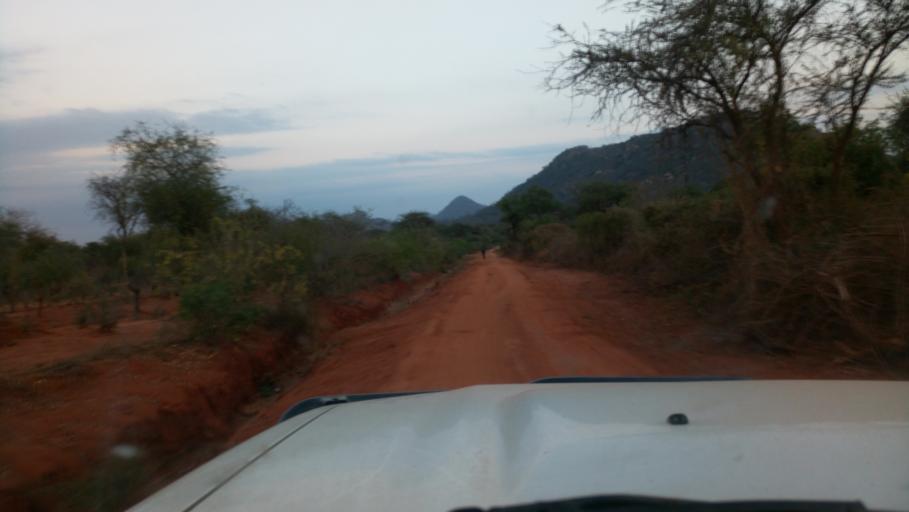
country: KE
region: Kitui
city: Kitui
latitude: -1.7336
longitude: 38.2024
